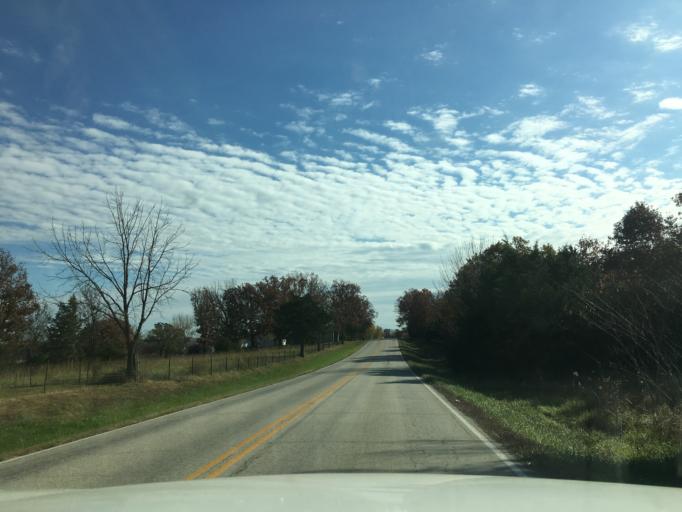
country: US
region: Missouri
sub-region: Maries County
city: Belle
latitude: 38.3540
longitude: -91.8000
